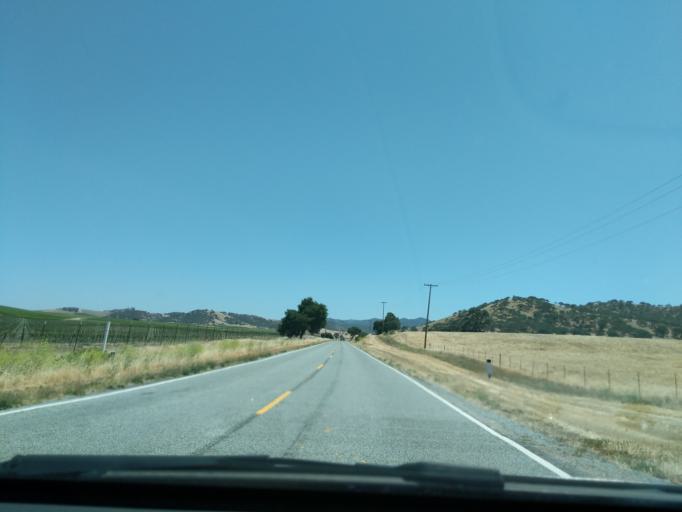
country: US
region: California
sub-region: Monterey County
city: King City
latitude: 36.1608
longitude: -121.1319
